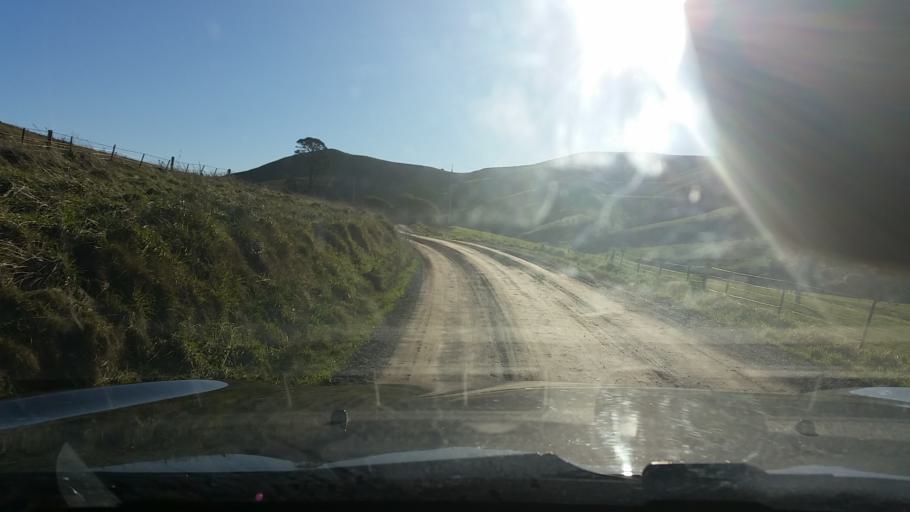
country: NZ
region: Marlborough
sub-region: Marlborough District
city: Blenheim
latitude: -41.5876
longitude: 174.0887
